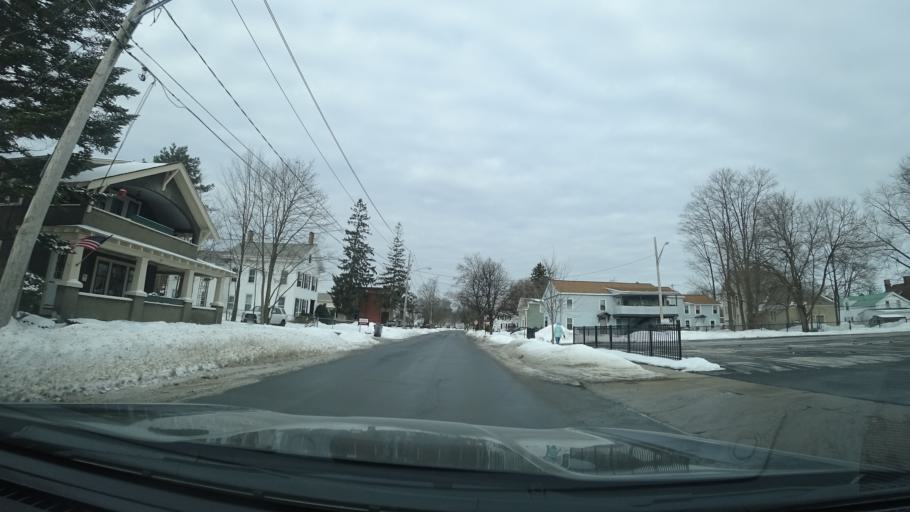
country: US
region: New York
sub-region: Warren County
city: Glens Falls
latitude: 43.3099
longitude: -73.6483
